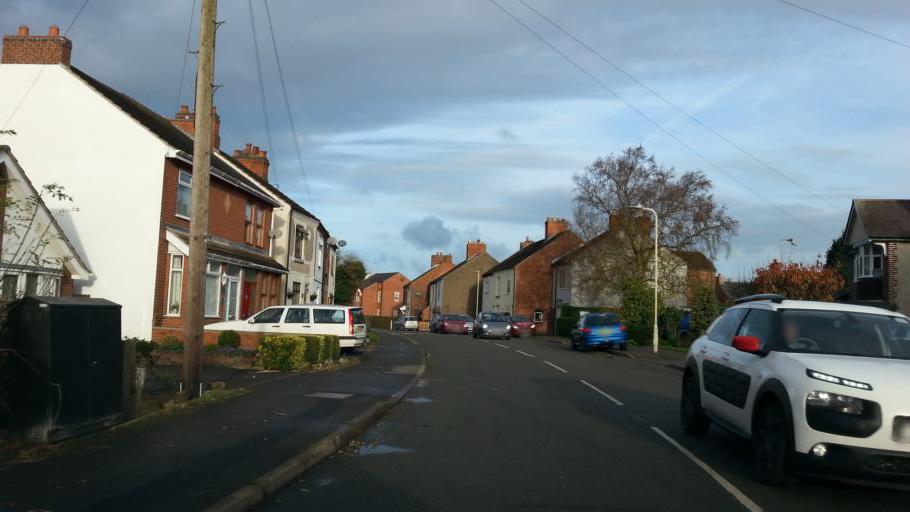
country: GB
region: England
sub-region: Leicestershire
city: Coalville
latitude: 52.7137
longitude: -1.3802
